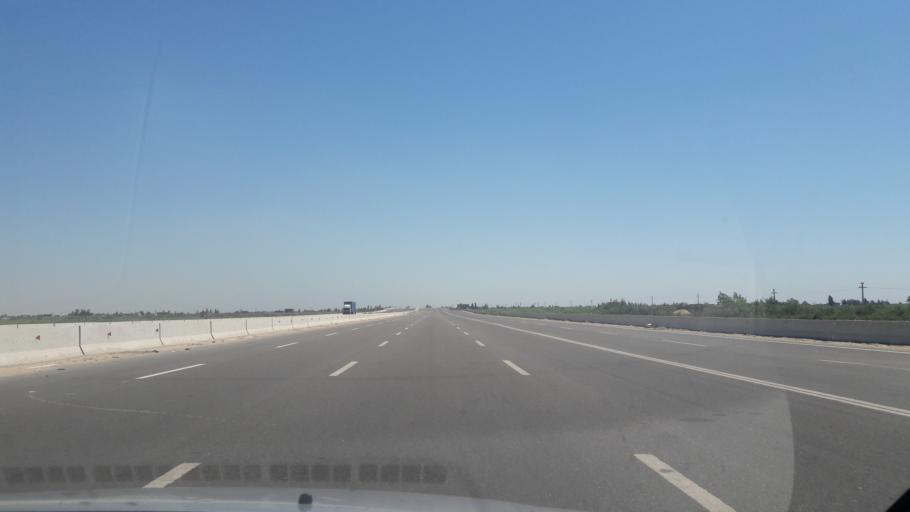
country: EG
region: Muhafazat Bur Sa`id
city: Port Said
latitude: 31.1519
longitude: 32.2350
